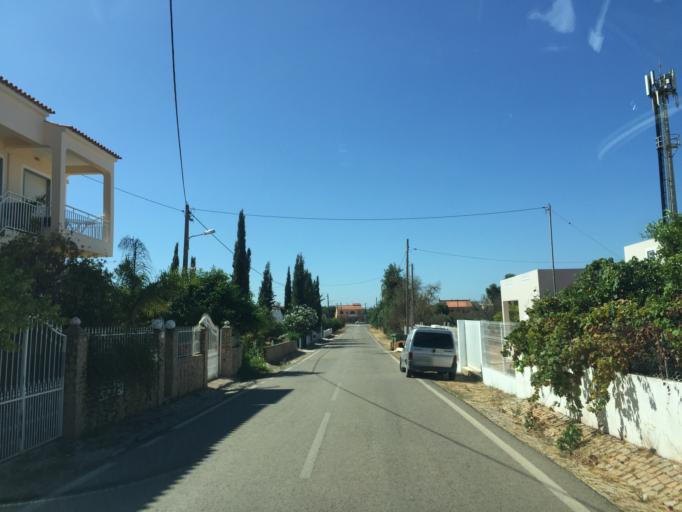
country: PT
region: Faro
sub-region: Loule
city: Vilamoura
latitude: 37.1133
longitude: -8.1001
